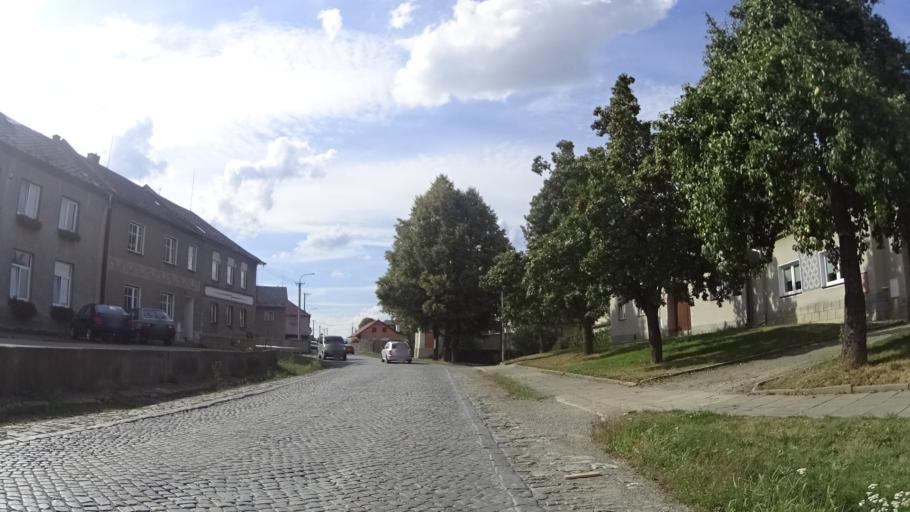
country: CZ
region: Olomoucky
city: Moravicany
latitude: 49.7578
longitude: 16.9584
